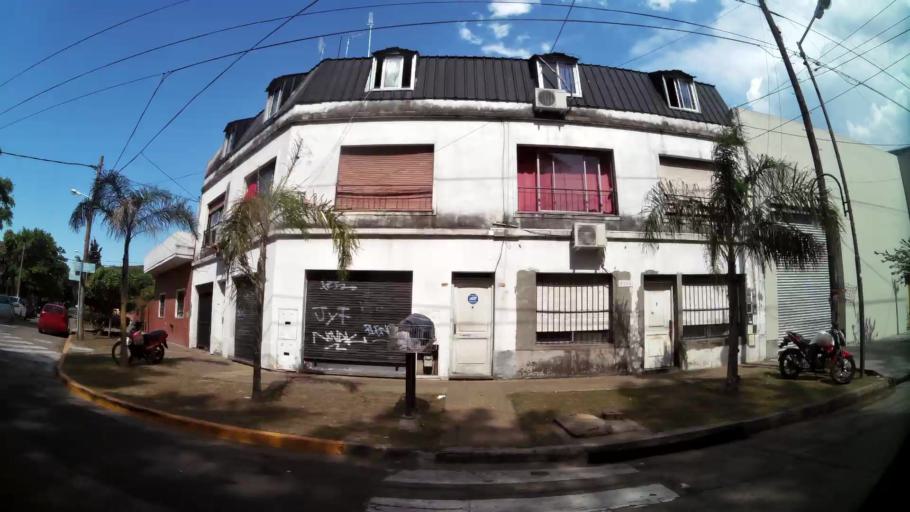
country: AR
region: Buenos Aires
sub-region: Partido de Tigre
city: Tigre
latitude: -34.4700
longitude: -58.5766
